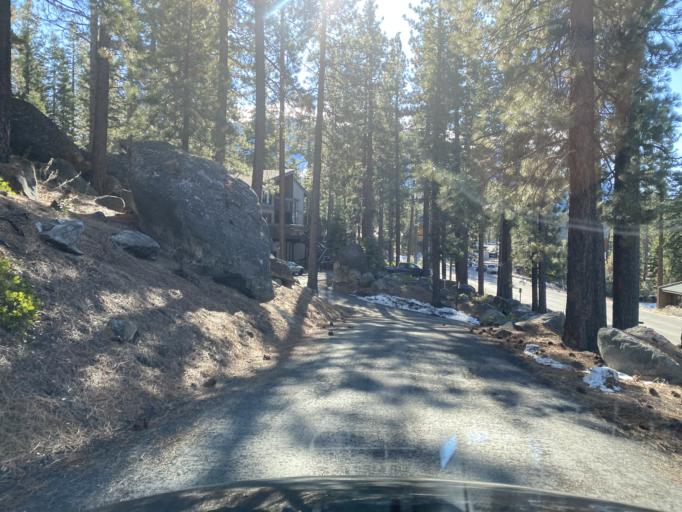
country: US
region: Nevada
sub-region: Douglas County
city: Kingsbury
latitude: 38.9744
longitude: -119.9344
